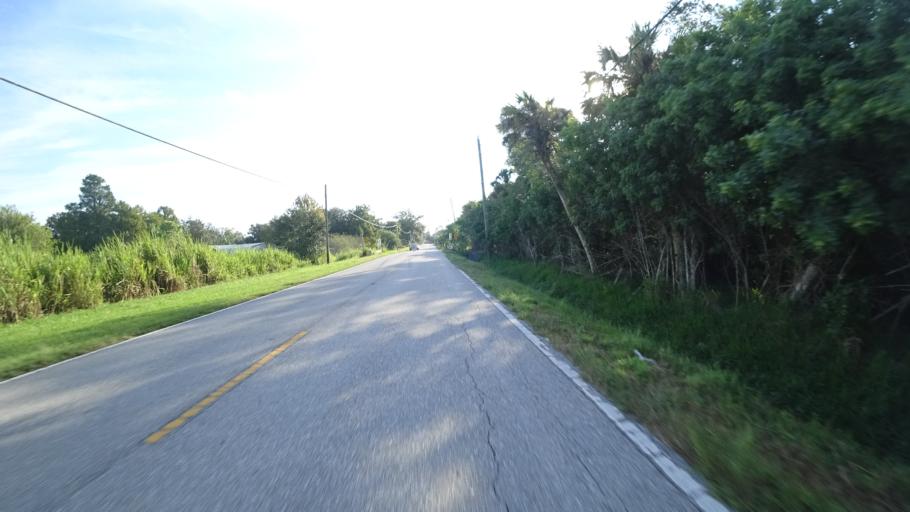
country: US
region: Florida
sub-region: Manatee County
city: Samoset
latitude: 27.4655
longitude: -82.5197
